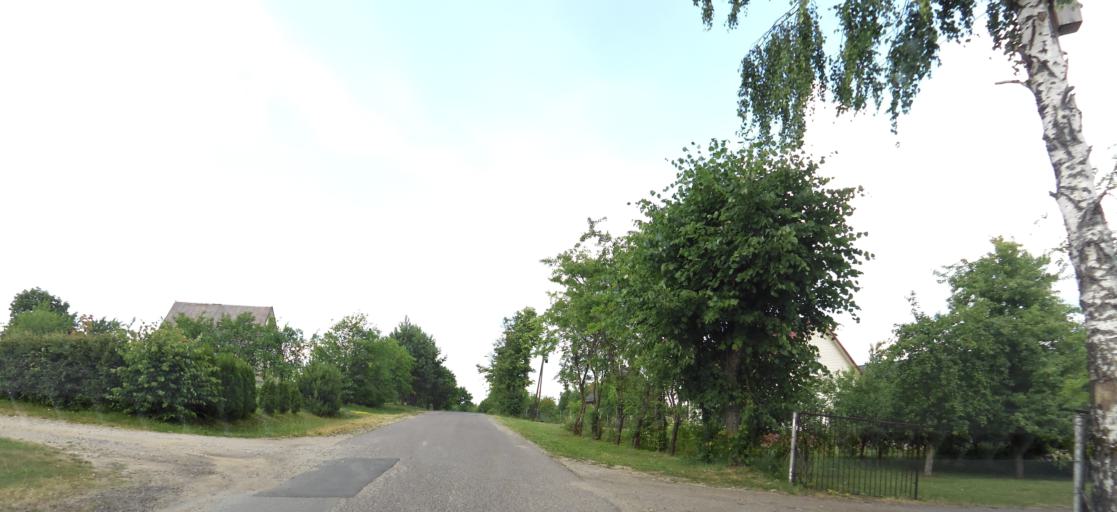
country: LT
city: Skaidiskes
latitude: 54.5326
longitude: 25.6489
